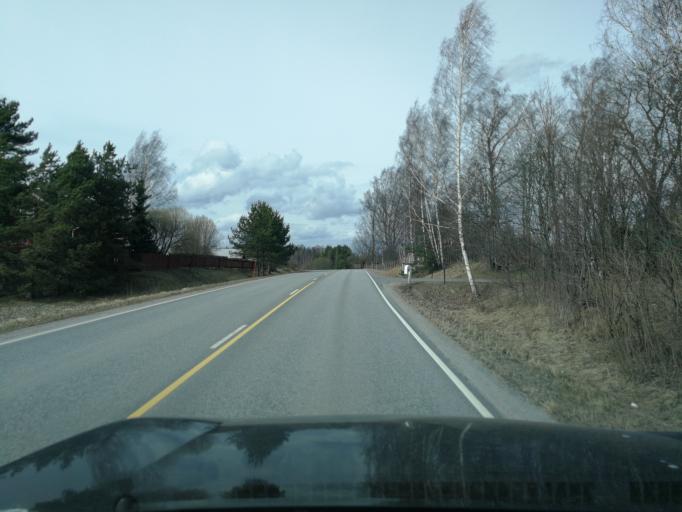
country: FI
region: Uusimaa
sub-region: Helsinki
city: Siuntio
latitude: 60.1254
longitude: 24.2356
